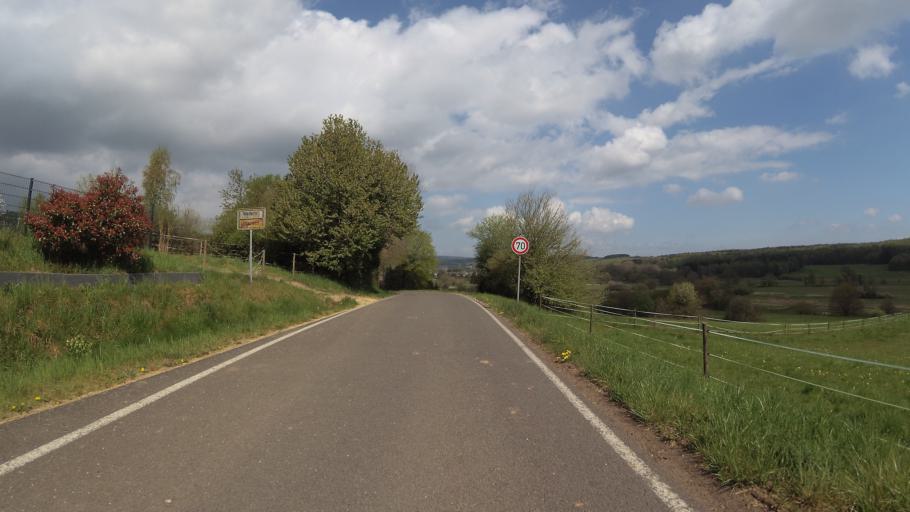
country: DE
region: Saarland
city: Wadern
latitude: 49.5506
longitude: 6.8882
